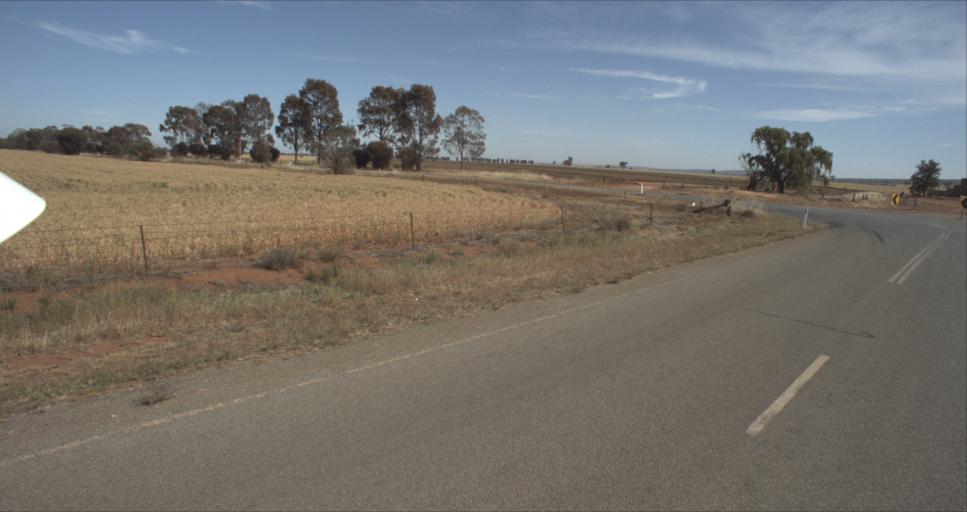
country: AU
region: New South Wales
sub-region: Leeton
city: Leeton
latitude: -34.5610
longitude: 146.4818
